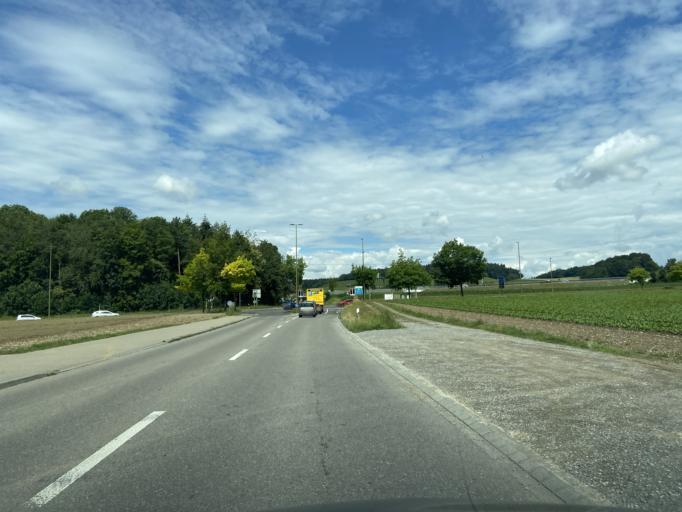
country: CH
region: Zurich
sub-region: Bezirk Winterthur
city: Oberwinterthur (Kreis 2)
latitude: 47.5281
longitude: 8.7737
